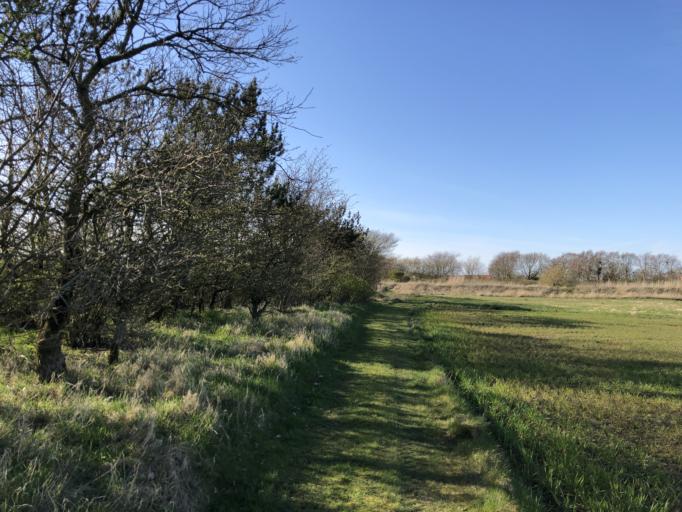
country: DK
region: Central Jutland
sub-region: Holstebro Kommune
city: Ulfborg
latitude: 56.3300
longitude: 8.3137
